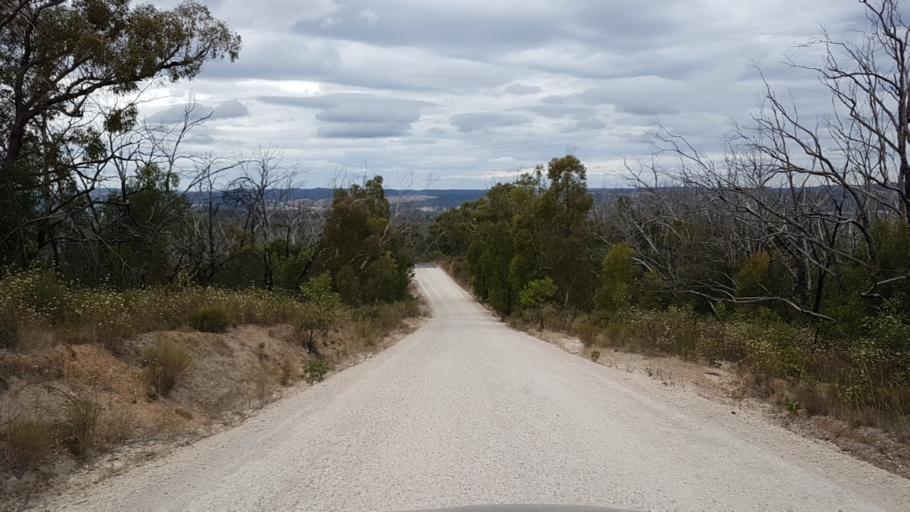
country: AU
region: South Australia
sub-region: Adelaide Hills
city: Gumeracha
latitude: -34.7734
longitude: 138.8186
